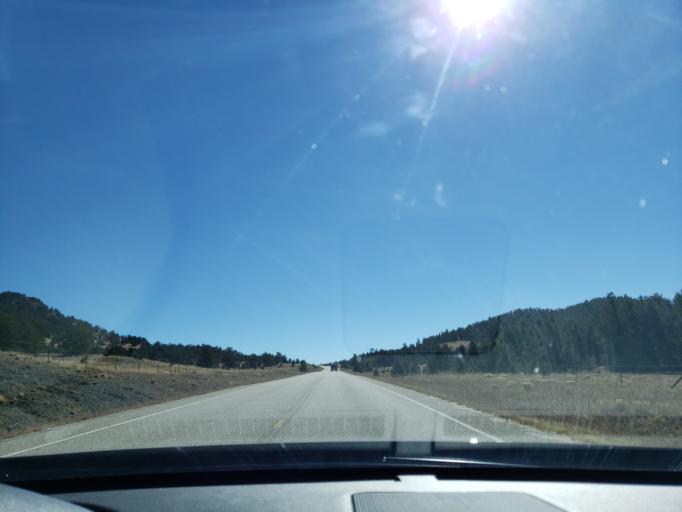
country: US
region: Colorado
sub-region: Chaffee County
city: Salida
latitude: 38.8441
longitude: -105.6423
